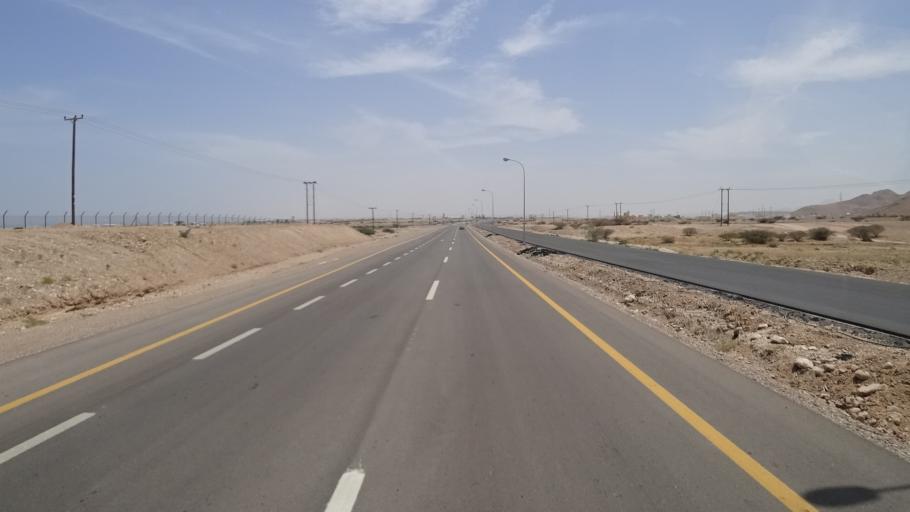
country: OM
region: Ash Sharqiyah
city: Sur
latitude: 22.6238
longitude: 59.4156
